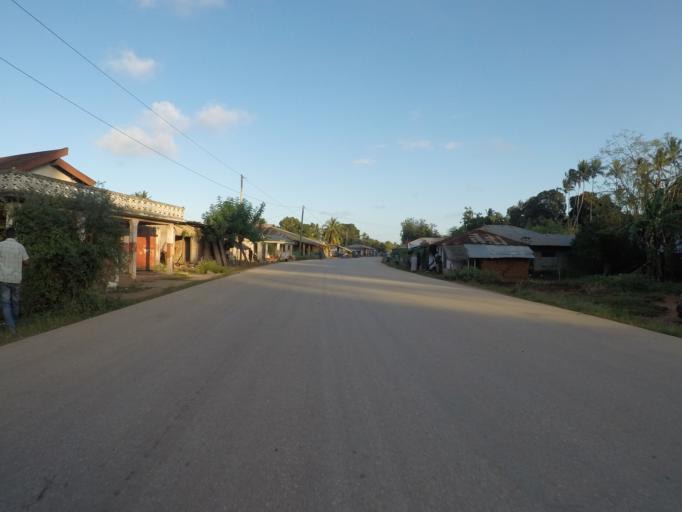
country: TZ
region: Zanzibar North
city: Gamba
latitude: -5.8851
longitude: 39.2862
